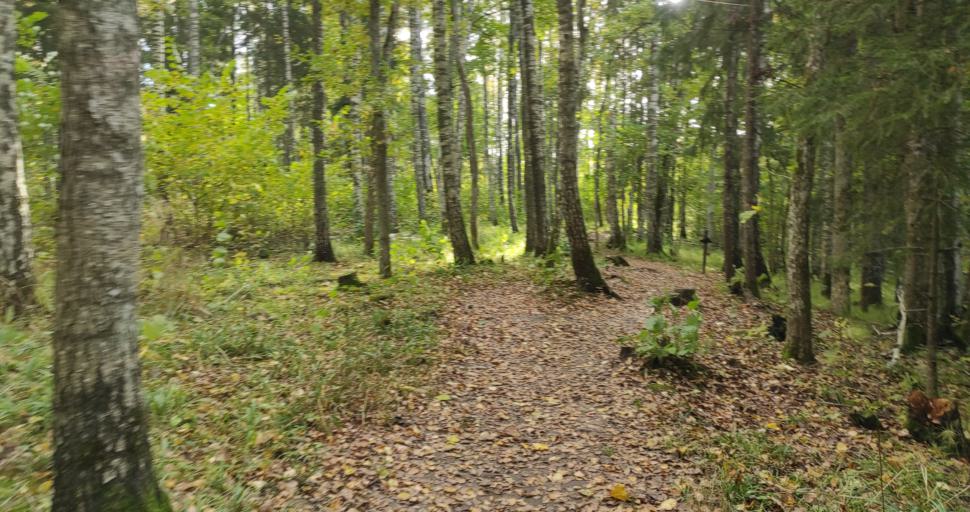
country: LV
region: Durbe
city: Liegi
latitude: 56.7325
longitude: 21.3710
